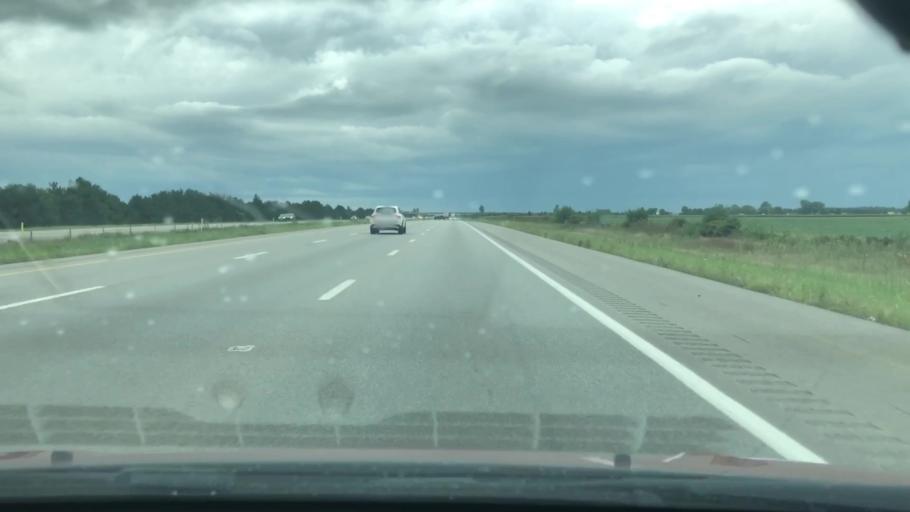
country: US
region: Ohio
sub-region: Wood County
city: Bowling Green
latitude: 41.4009
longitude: -83.6157
